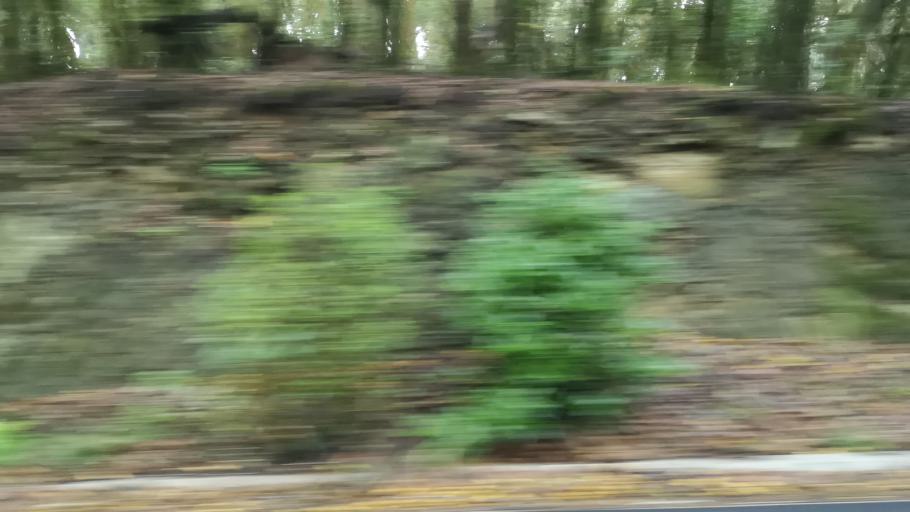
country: ES
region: Canary Islands
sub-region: Provincia de Santa Cruz de Tenerife
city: Vallehermosa
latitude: 28.1474
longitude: -17.2903
